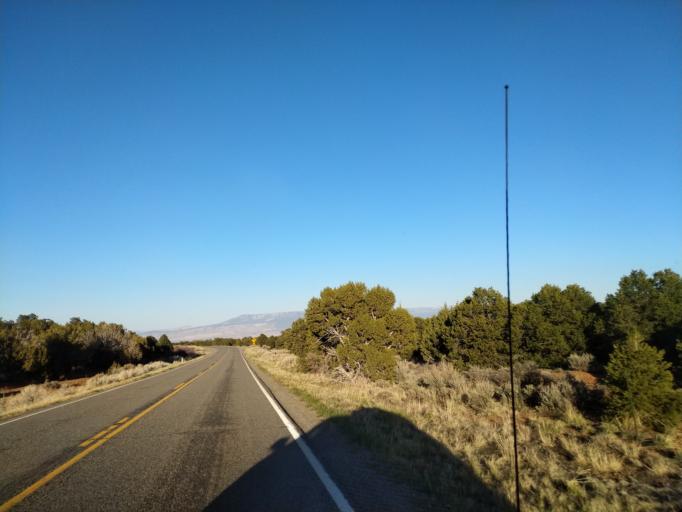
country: US
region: Colorado
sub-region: Mesa County
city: Redlands
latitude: 39.0098
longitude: -108.6775
